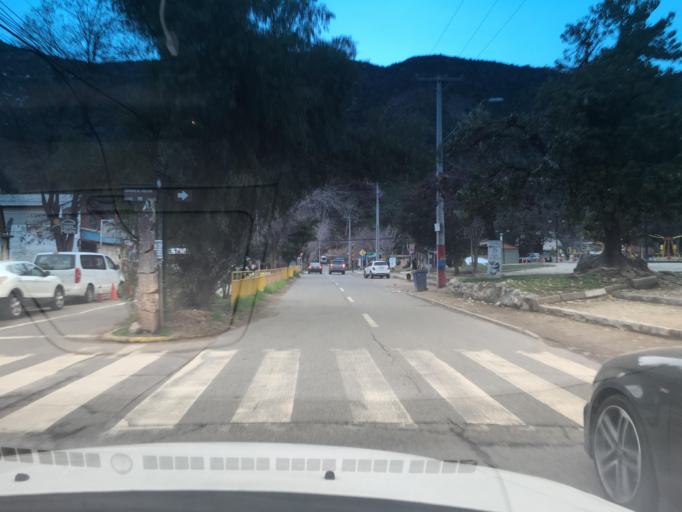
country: CL
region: Santiago Metropolitan
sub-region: Provincia de Cordillera
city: Puente Alto
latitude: -33.6443
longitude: -70.3538
